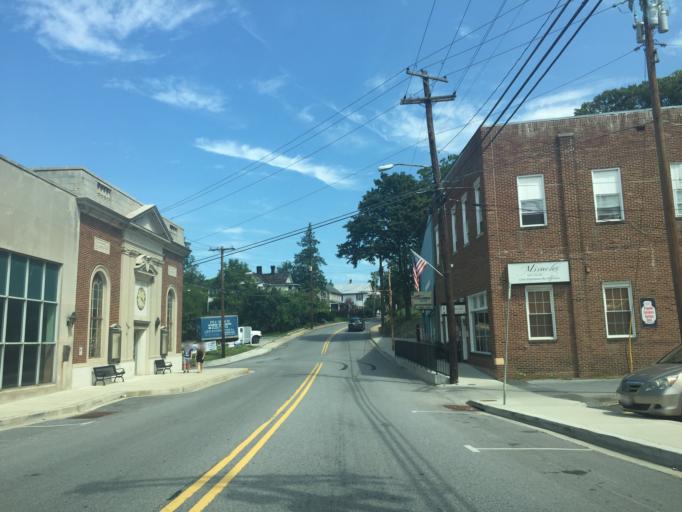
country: US
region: Maryland
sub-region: Carroll County
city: Mount Airy
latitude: 39.3772
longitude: -77.1542
